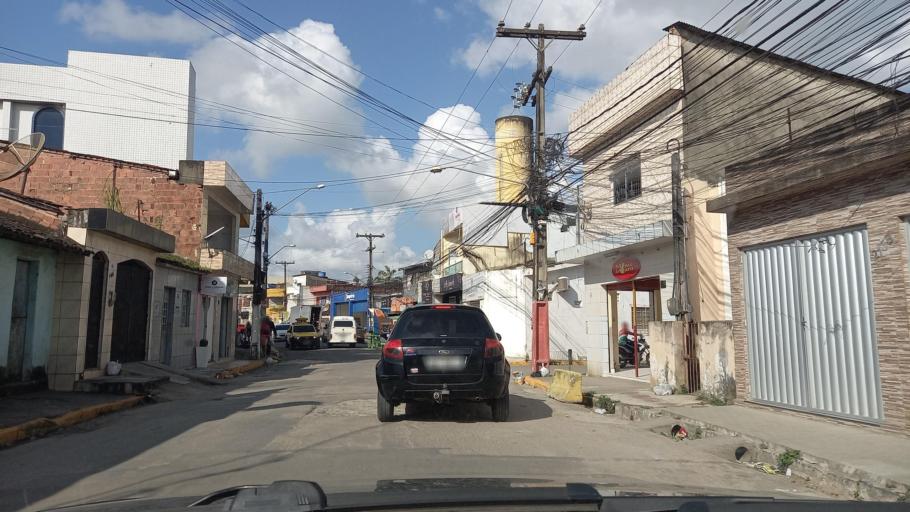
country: BR
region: Pernambuco
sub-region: Goiana
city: Goiana
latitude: -7.5603
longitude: -35.0034
